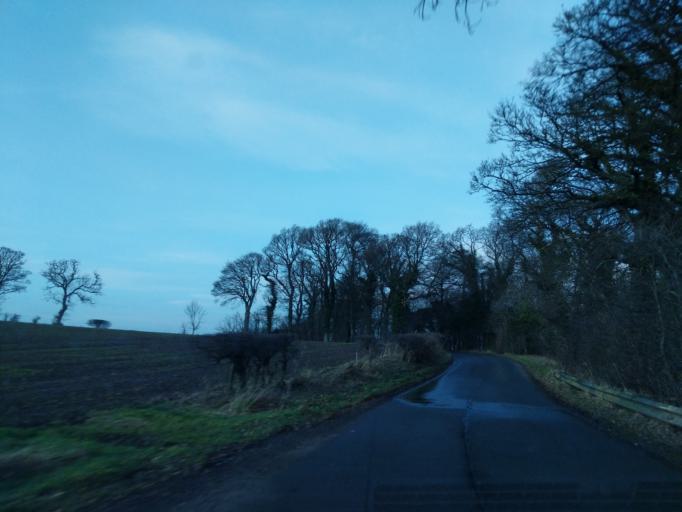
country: GB
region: Scotland
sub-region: Midlothian
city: Bonnyrigg
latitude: 55.8453
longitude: -3.0912
